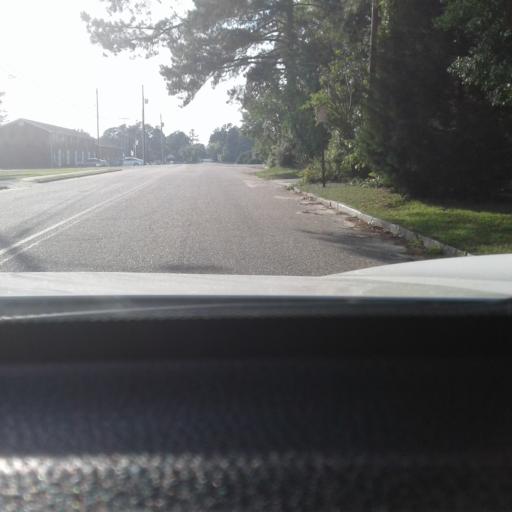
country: US
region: North Carolina
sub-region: Harnett County
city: Dunn
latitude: 35.3131
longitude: -78.6143
